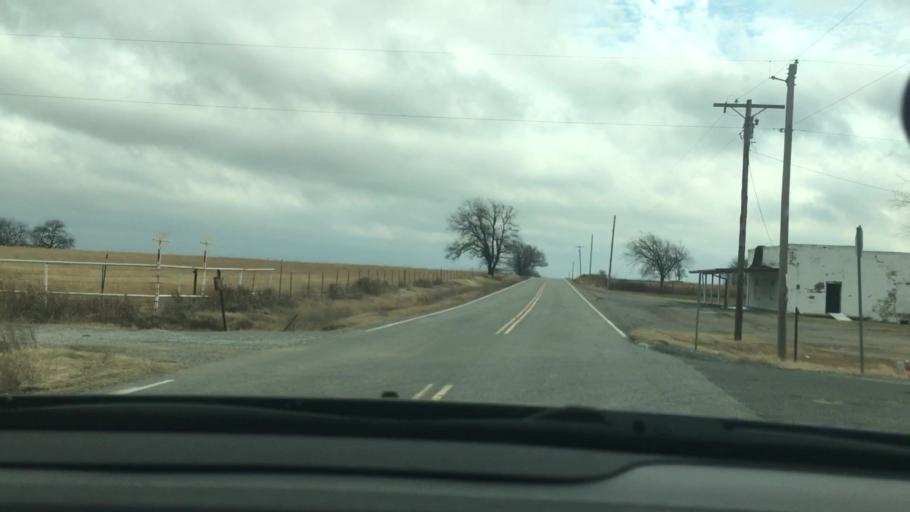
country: US
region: Oklahoma
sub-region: Bryan County
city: Durant
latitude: 34.0887
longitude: -96.4792
